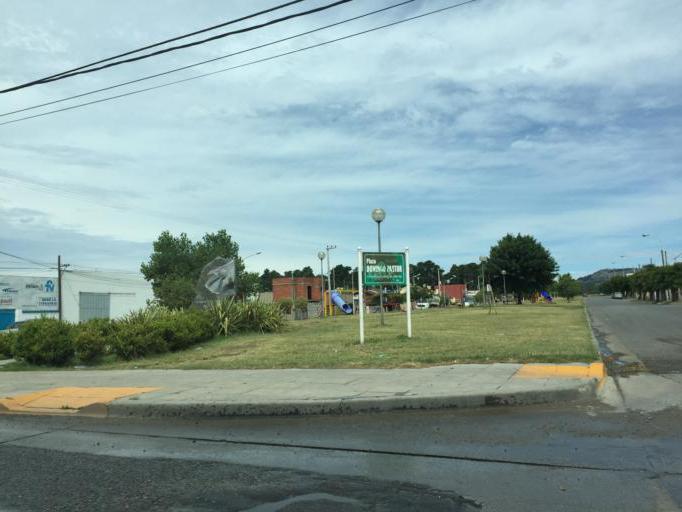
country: AR
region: Buenos Aires
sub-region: Partido de Tandil
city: Tandil
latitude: -37.3212
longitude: -59.1074
